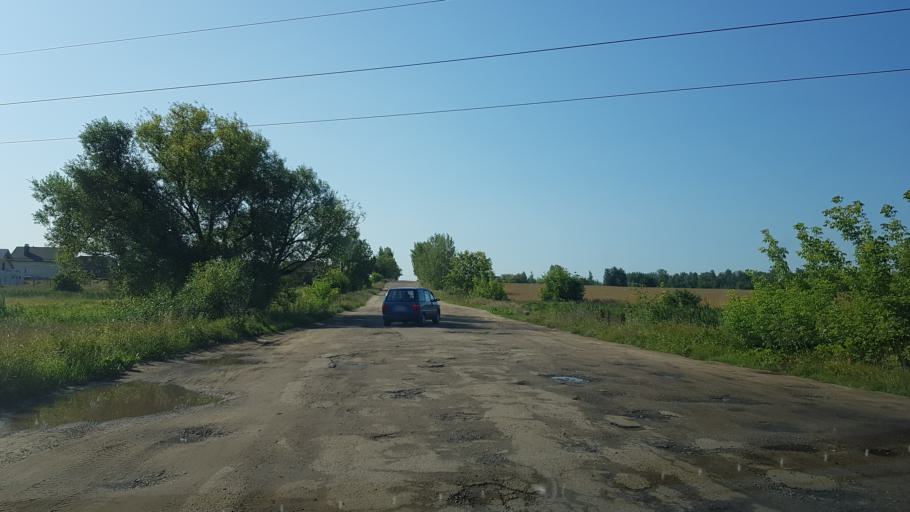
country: BY
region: Mogilev
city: Babruysk
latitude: 53.1145
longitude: 29.1905
